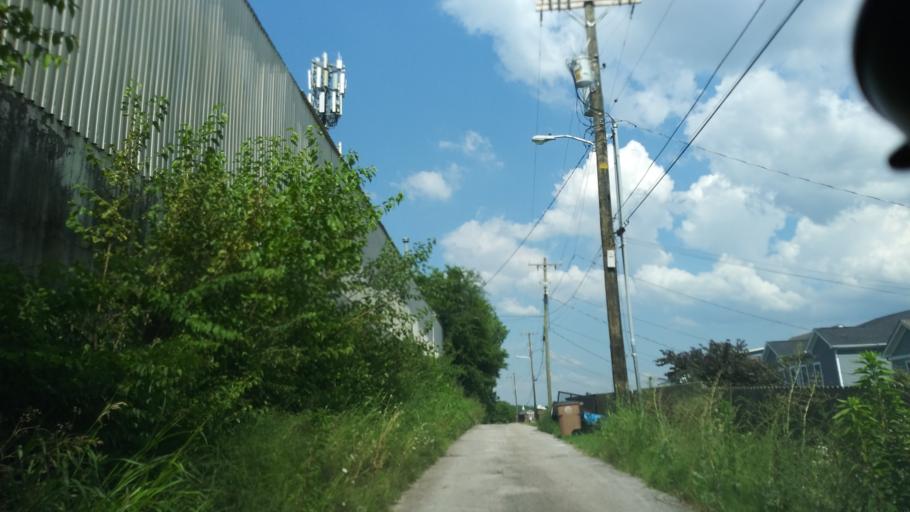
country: US
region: Tennessee
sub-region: Davidson County
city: Nashville
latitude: 36.1595
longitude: -86.8426
